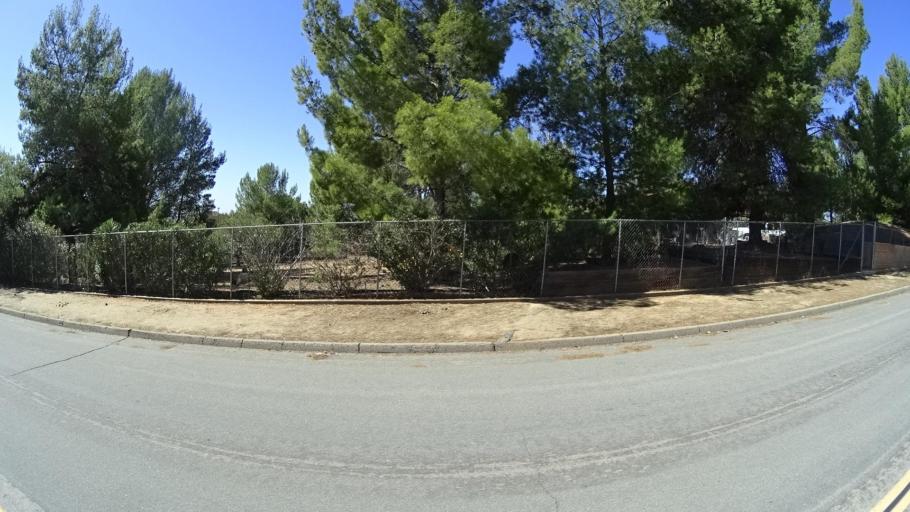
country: US
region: California
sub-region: San Diego County
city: Harbison Canyon
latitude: 32.8746
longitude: -116.8313
